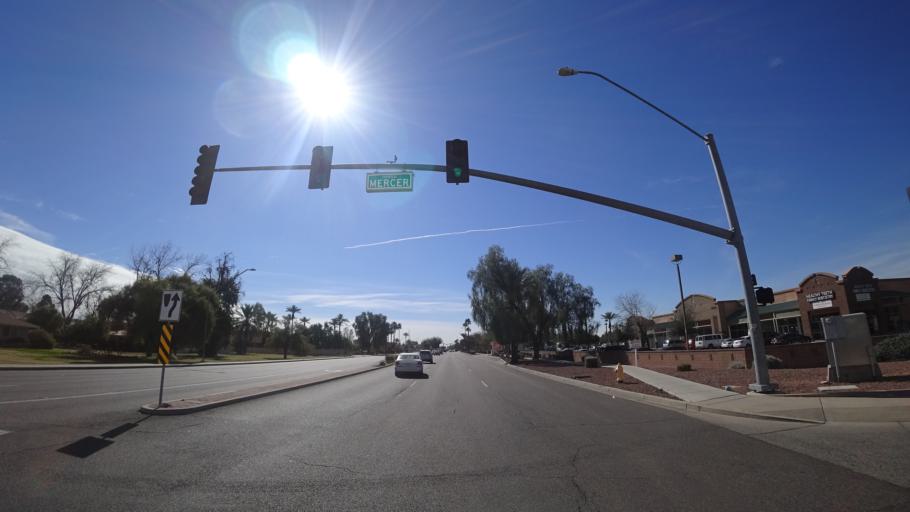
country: US
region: Arizona
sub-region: Maricopa County
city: Glendale
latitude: 33.5848
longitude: -112.1862
